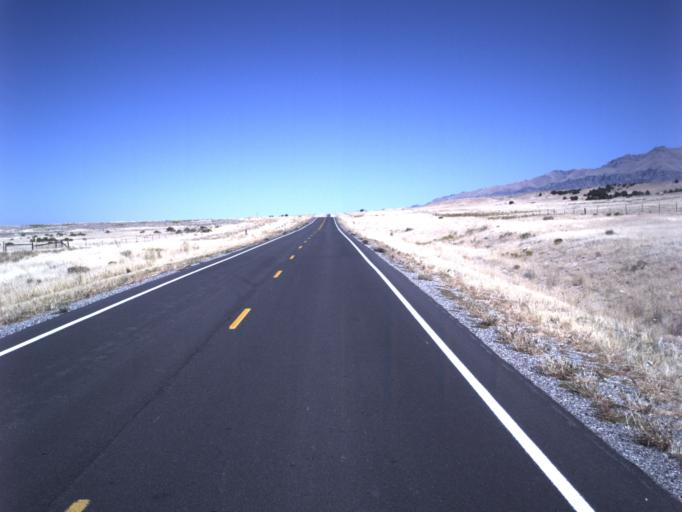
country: US
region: Utah
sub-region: Tooele County
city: Grantsville
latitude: 40.5633
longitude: -112.7341
